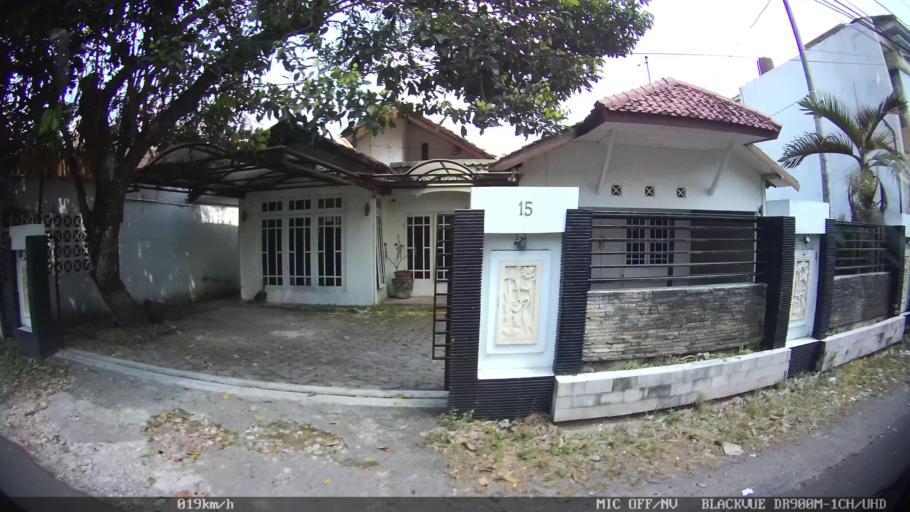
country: ID
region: Daerah Istimewa Yogyakarta
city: Yogyakarta
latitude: -7.7985
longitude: 110.3941
